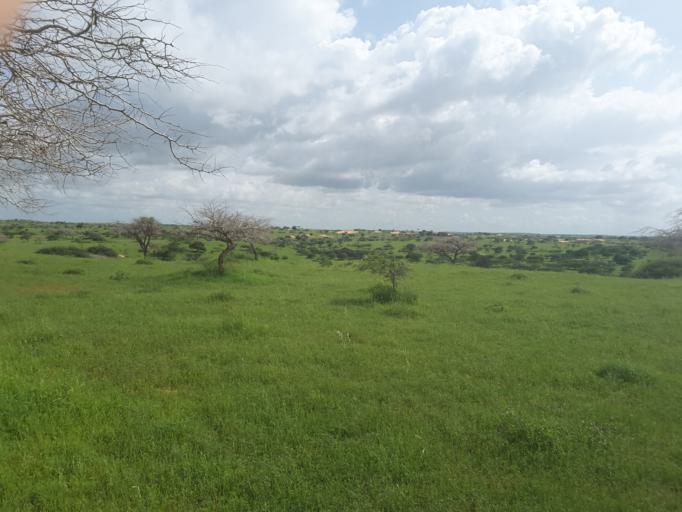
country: SN
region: Thies
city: Mekhe
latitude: 15.3513
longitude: -16.7223
